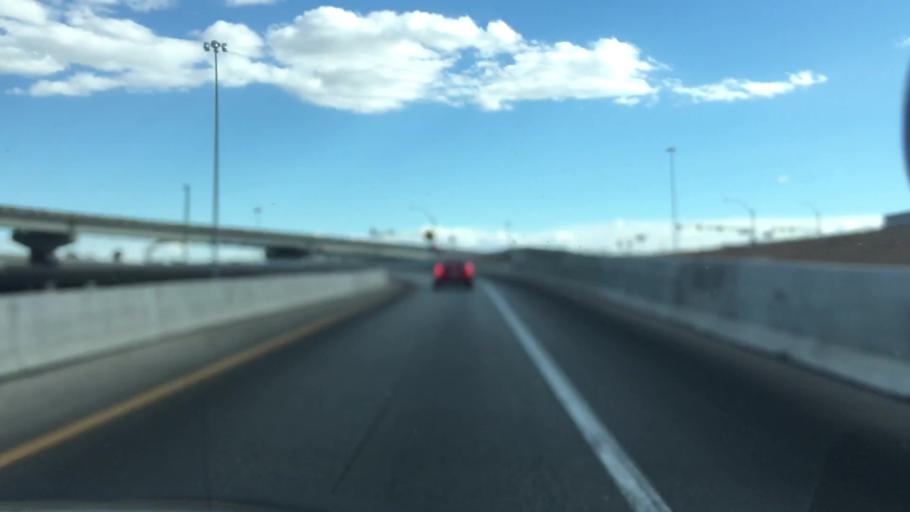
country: US
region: Nevada
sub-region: Clark County
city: Spring Valley
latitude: 36.1771
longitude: -115.2459
